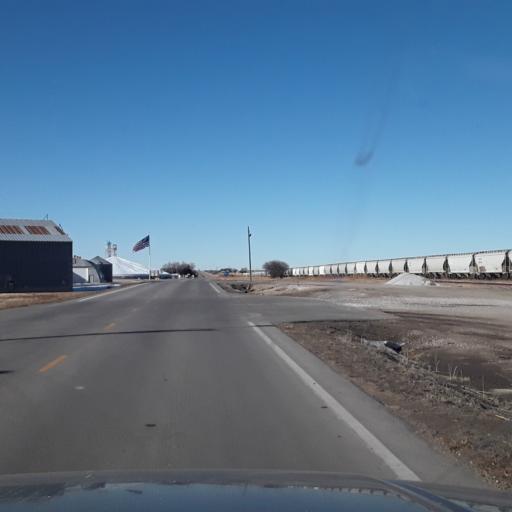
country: US
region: Nebraska
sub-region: Gosper County
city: Elwood
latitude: 40.5291
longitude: -99.6361
